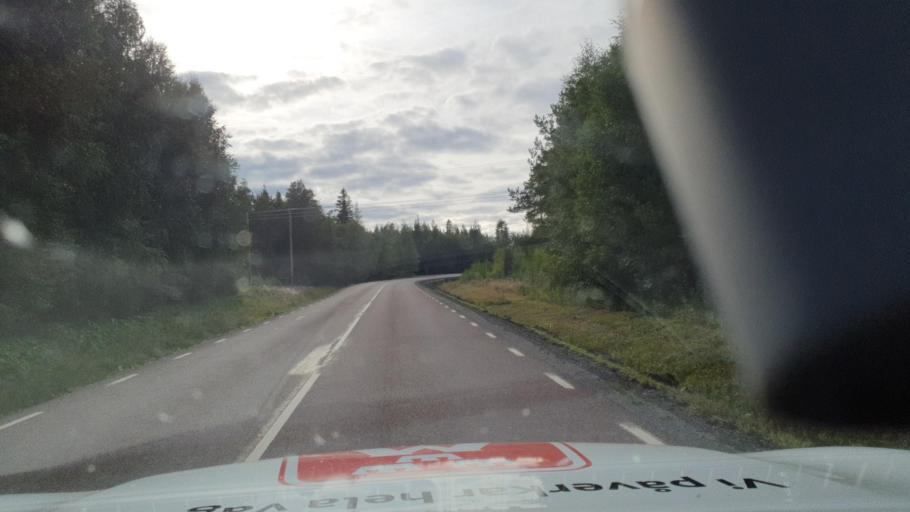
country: SE
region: Jaemtland
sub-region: Stroemsunds Kommun
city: Stroemsund
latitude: 63.8166
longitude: 15.6295
